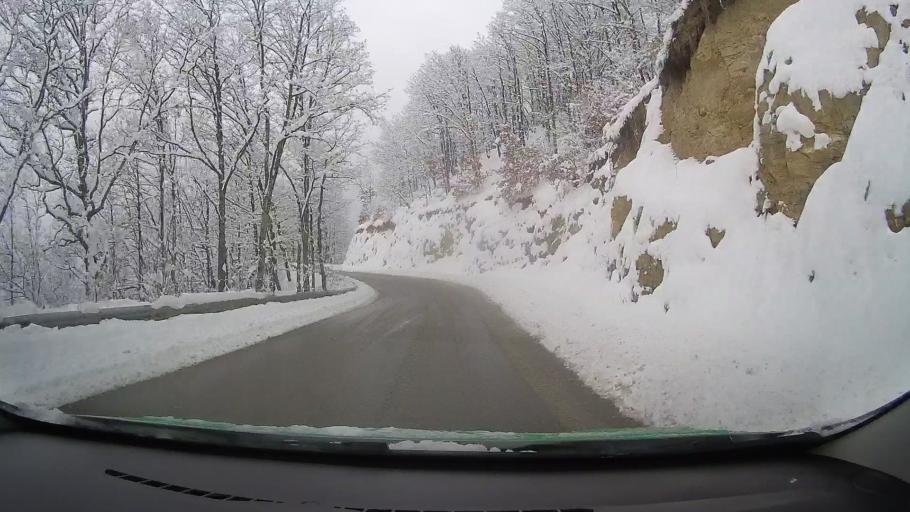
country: RO
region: Alba
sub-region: Comuna Sugag
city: Dobra
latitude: 45.7633
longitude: 23.6661
